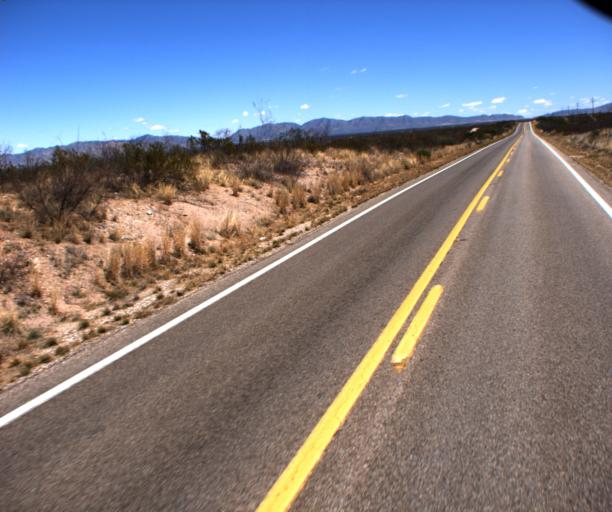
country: US
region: Arizona
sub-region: Cochise County
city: Tombstone
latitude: 31.7466
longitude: -110.1209
